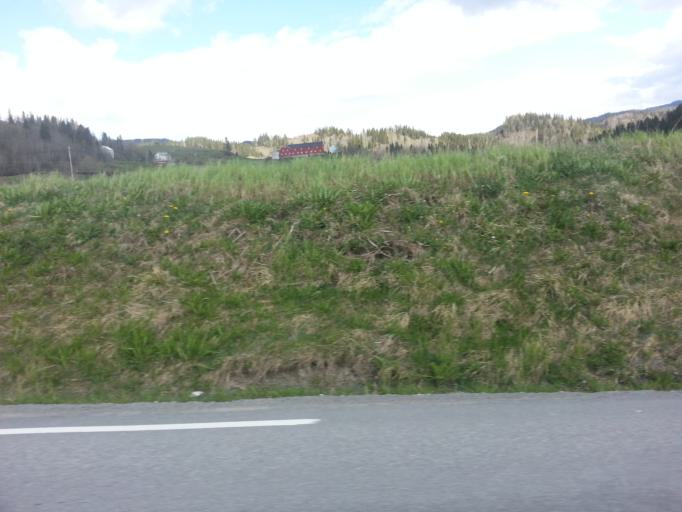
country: NO
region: Nord-Trondelag
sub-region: Levanger
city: Skogn
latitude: 63.6388
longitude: 11.2622
